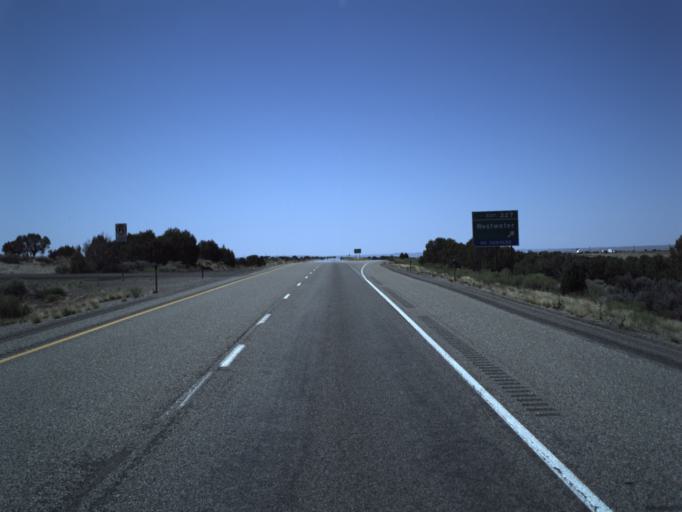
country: US
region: Colorado
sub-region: Mesa County
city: Loma
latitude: 39.1796
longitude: -109.1231
